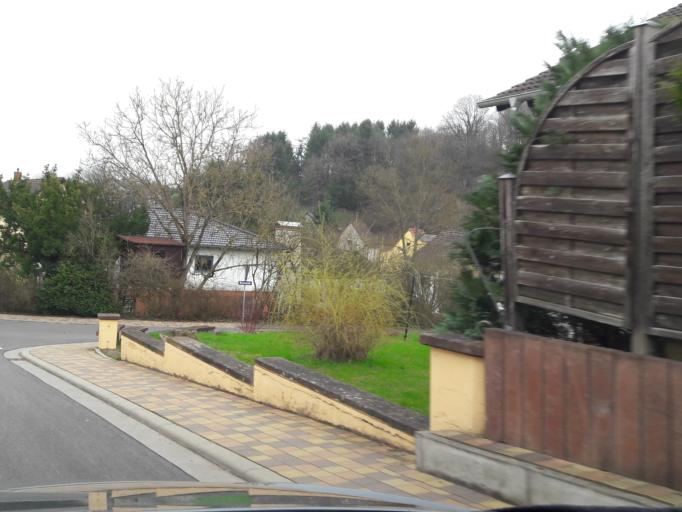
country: DE
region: Rheinland-Pfalz
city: Nanzdietschweiler
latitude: 49.4404
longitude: 7.4430
